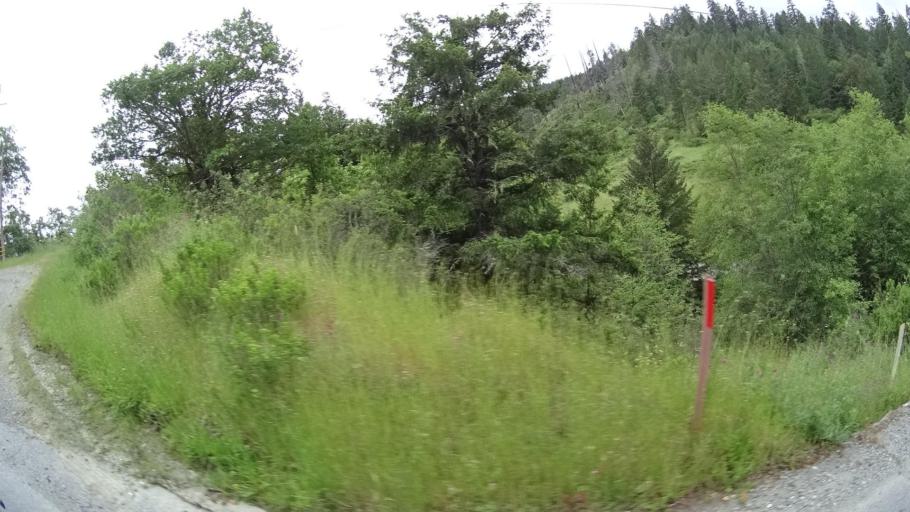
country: US
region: California
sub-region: Humboldt County
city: Willow Creek
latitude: 41.1021
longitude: -123.7109
